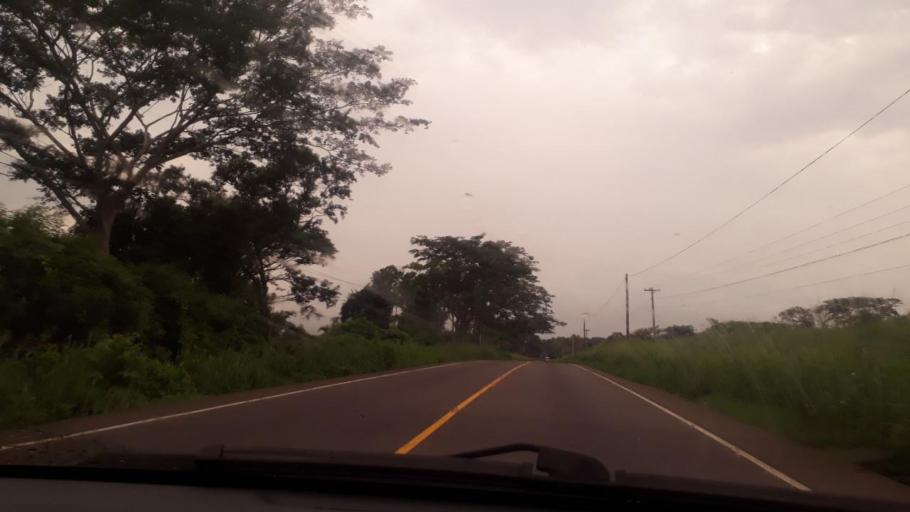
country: GT
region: Escuintla
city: Guanagazapa
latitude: 14.1313
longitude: -90.6495
